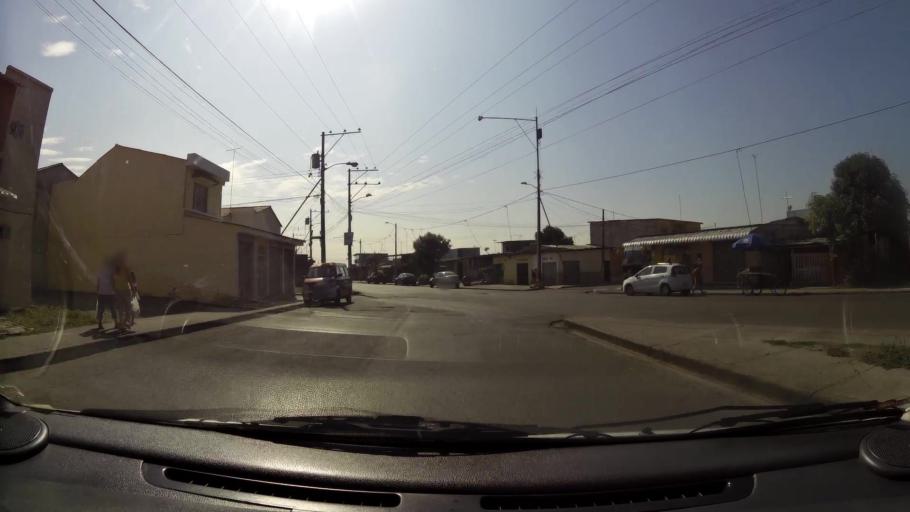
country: EC
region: Guayas
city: Eloy Alfaro
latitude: -2.0981
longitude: -79.9176
